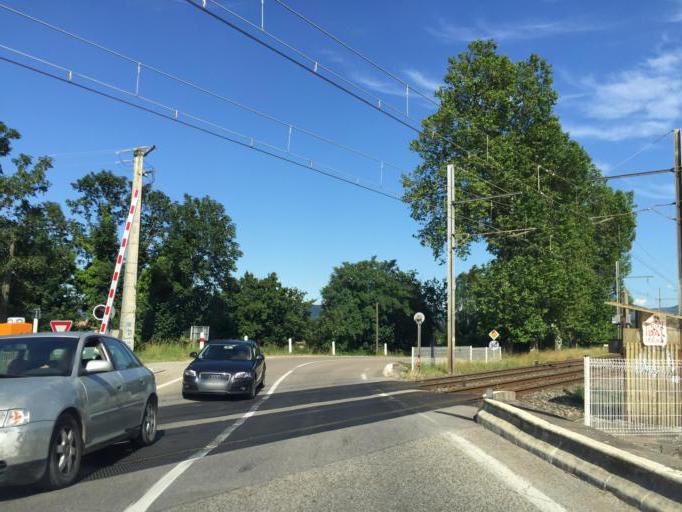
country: FR
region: Rhone-Alpes
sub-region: Departement de l'Ardeche
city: Le Pouzin
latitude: 44.7205
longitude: 4.7500
